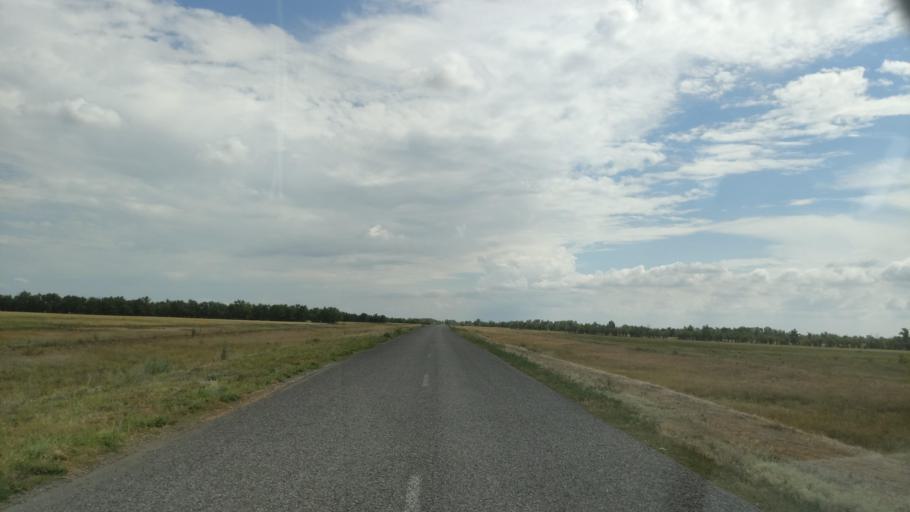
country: KZ
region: Pavlodar
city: Pavlodar
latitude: 52.6367
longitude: 76.9729
